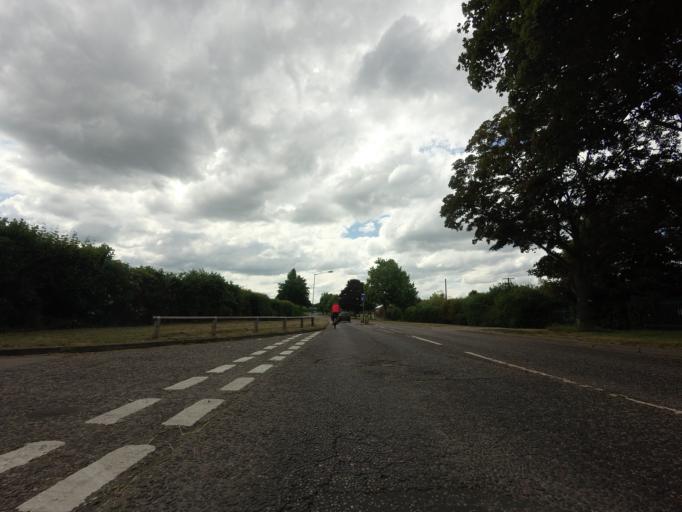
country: GB
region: England
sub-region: Kent
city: Hoo
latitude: 51.4204
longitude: 0.5468
